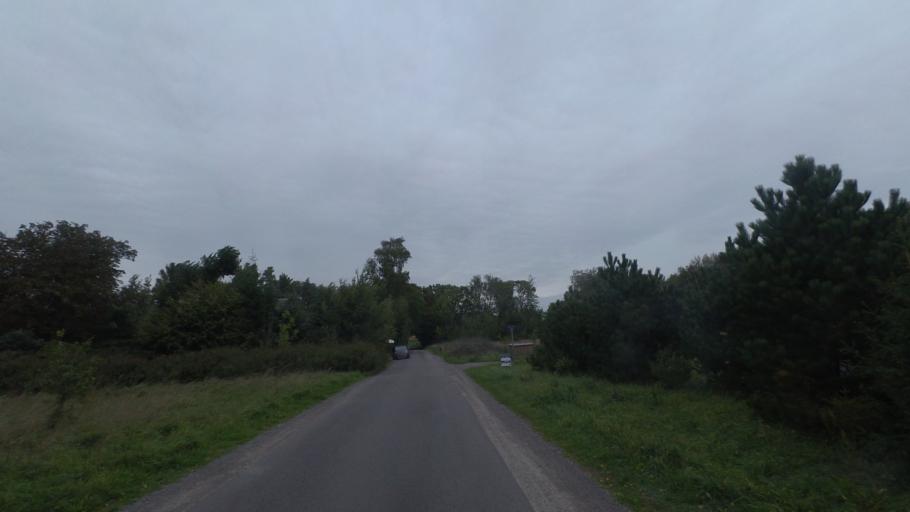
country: DK
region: Capital Region
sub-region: Bornholm Kommune
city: Akirkeby
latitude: 55.0037
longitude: 14.9923
